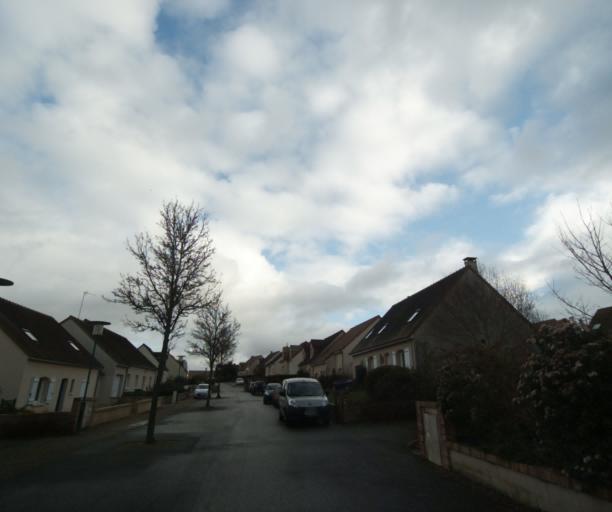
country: FR
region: Pays de la Loire
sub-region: Departement de la Sarthe
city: La Chapelle-Saint-Aubin
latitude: 48.0113
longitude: 0.1653
